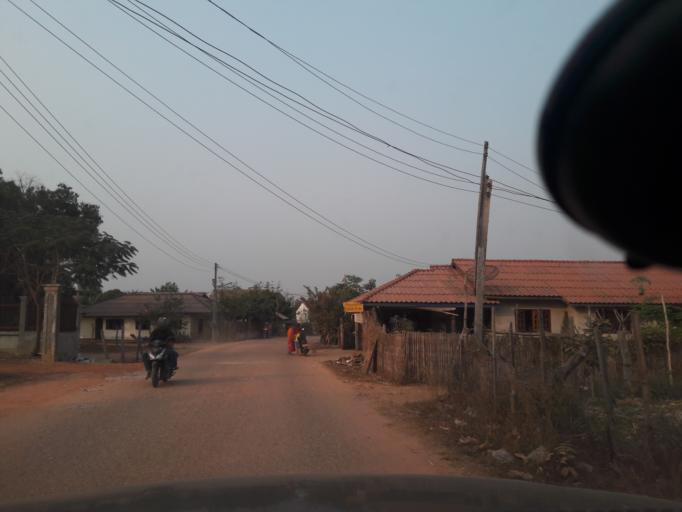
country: LA
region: Vientiane
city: Vientiane
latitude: 18.0621
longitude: 102.5275
